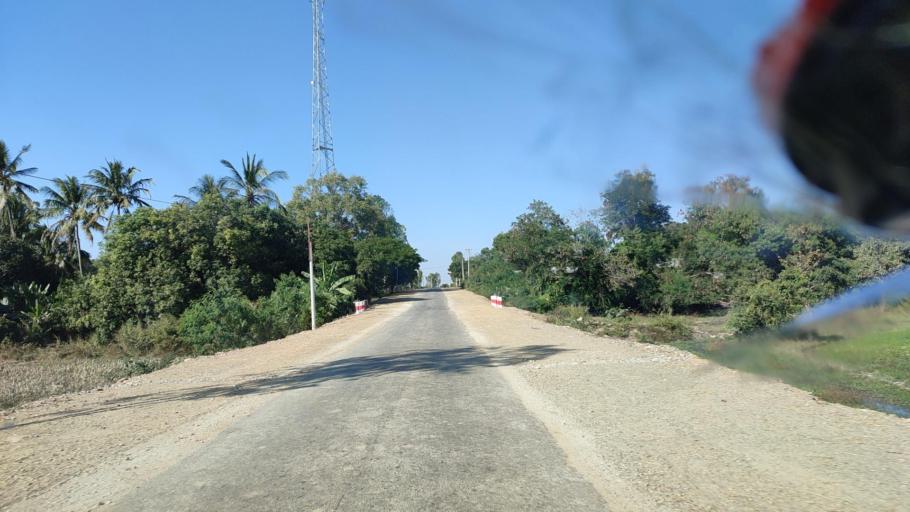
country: MM
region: Mandalay
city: Pyinmana
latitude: 20.0847
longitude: 96.2648
